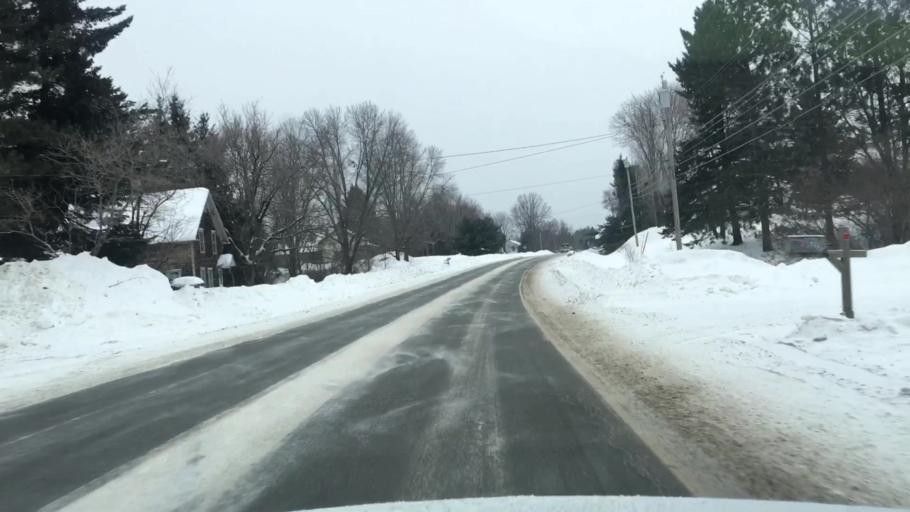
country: US
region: Maine
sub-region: Penobscot County
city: Lincoln
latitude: 45.4011
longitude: -68.4905
